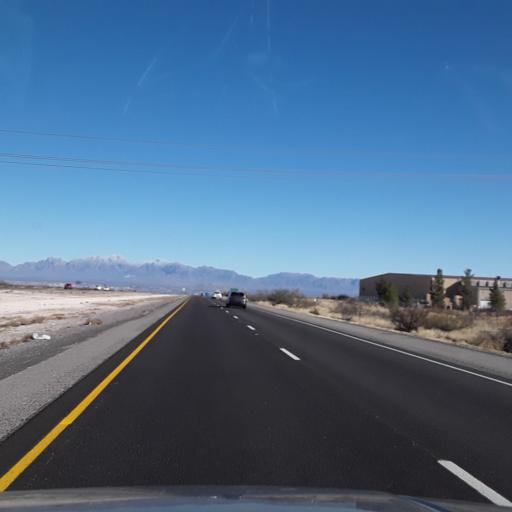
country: US
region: New Mexico
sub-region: Dona Ana County
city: Mesilla
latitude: 32.2725
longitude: -106.9165
